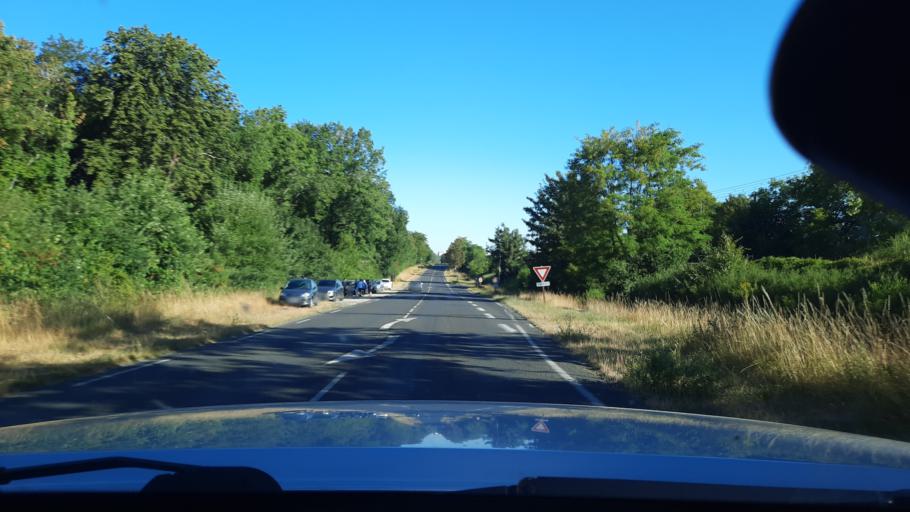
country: FR
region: Ile-de-France
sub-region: Departement de Seine-et-Marne
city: Livry-sur-Seine
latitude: 48.5042
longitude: 2.6833
